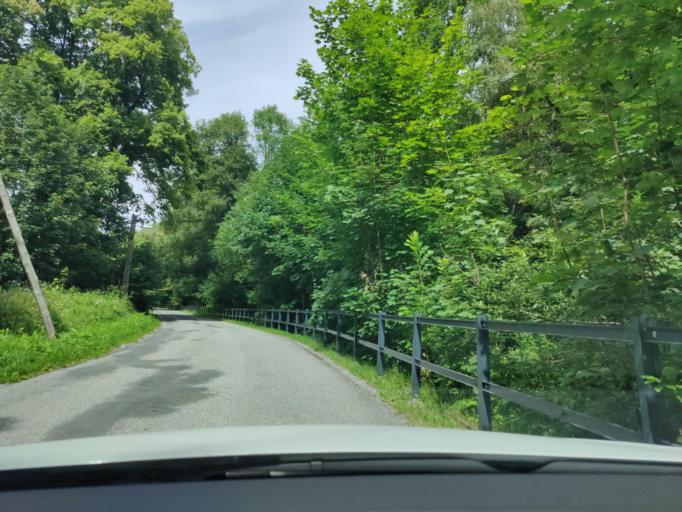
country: CZ
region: Olomoucky
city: Zlate Hory
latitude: 50.2246
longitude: 17.3452
